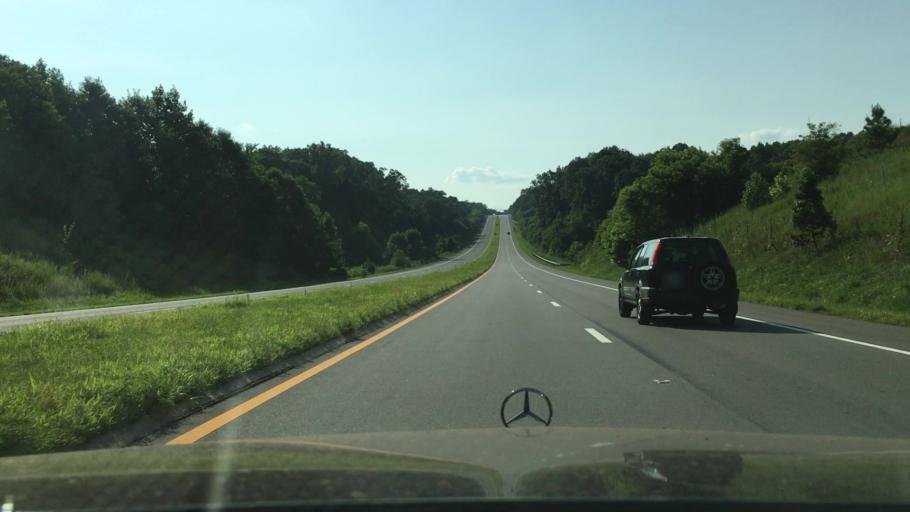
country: US
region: Virginia
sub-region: Amherst County
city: Madison Heights
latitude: 37.4151
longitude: -79.1098
